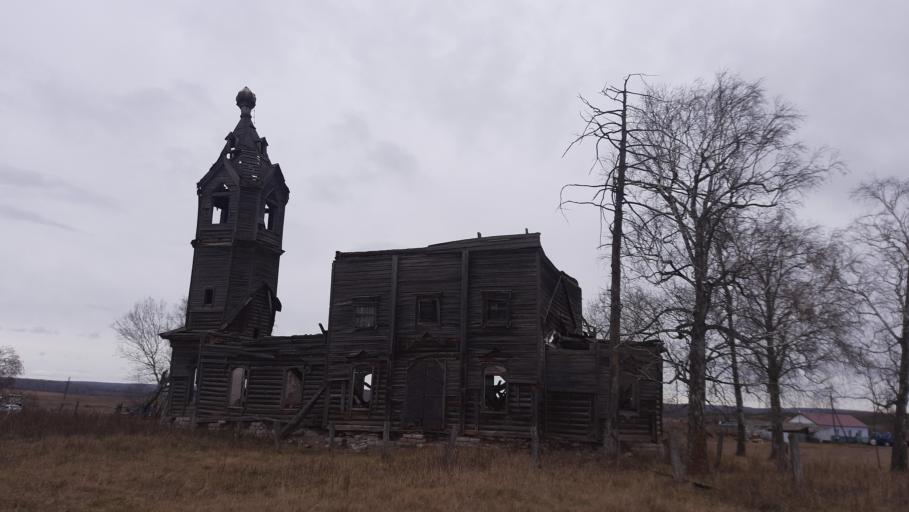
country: RU
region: Chelyabinsk
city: Kropachevo
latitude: 55.1044
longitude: 57.9653
